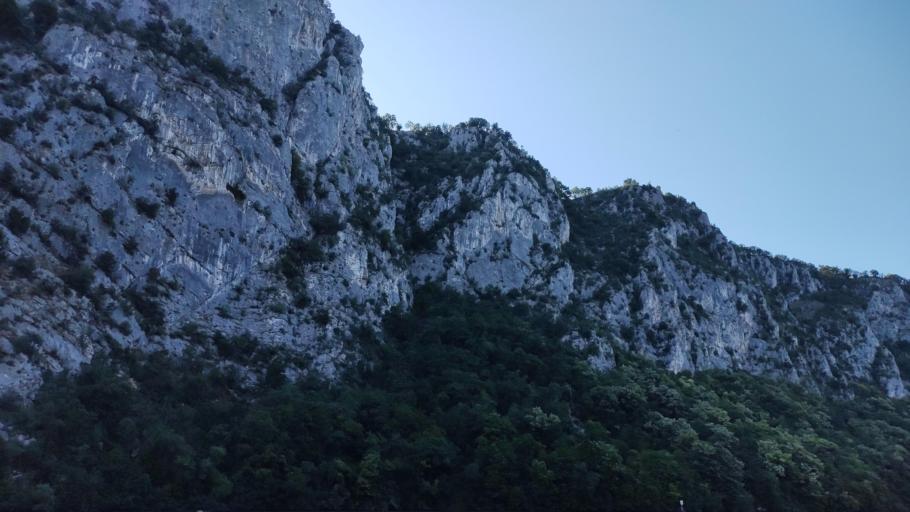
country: RO
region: Mehedinti
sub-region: Comuna Dubova
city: Dubova
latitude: 44.6010
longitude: 22.2656
